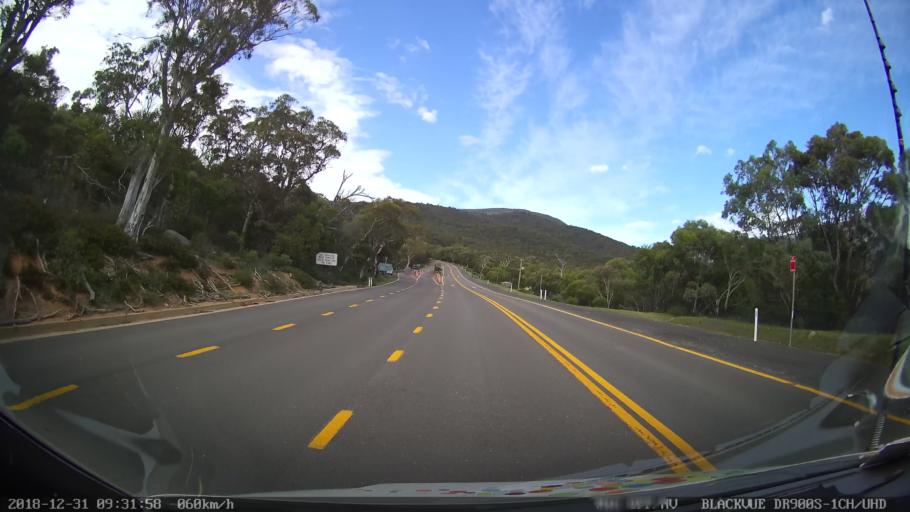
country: AU
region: New South Wales
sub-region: Snowy River
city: Jindabyne
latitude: -36.4499
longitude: 148.4384
